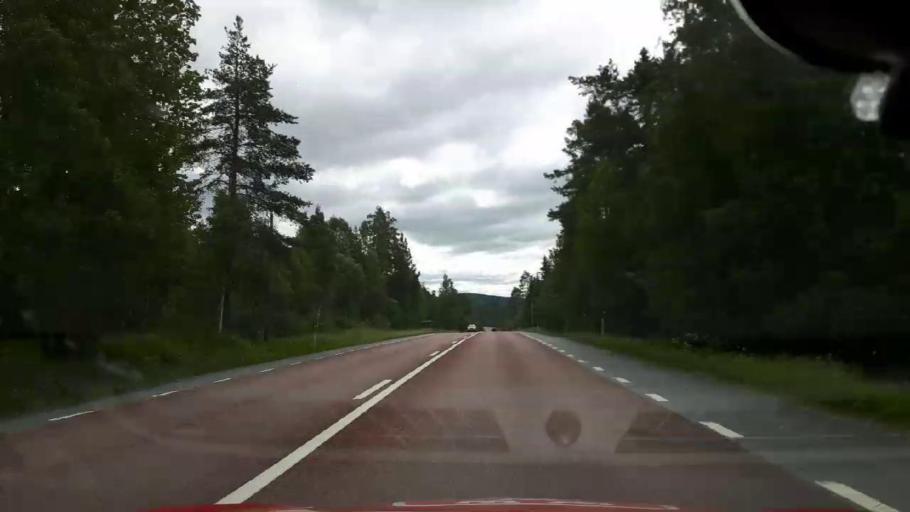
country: SE
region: Jaemtland
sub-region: Braecke Kommun
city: Braecke
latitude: 62.8244
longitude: 15.3242
